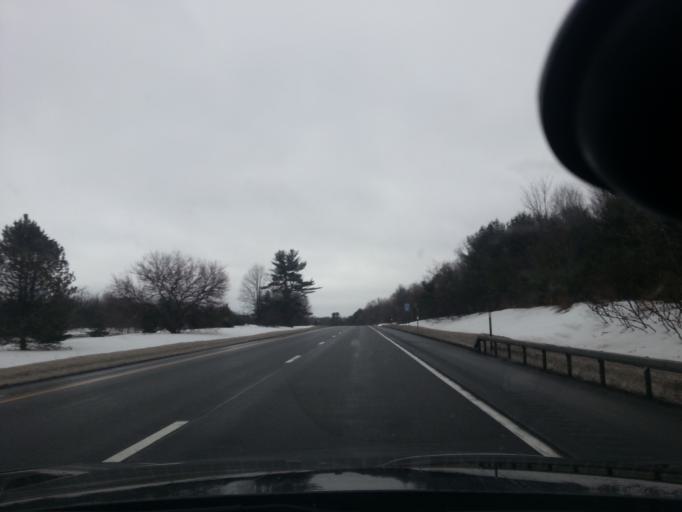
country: US
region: New York
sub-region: Oswego County
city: Central Square
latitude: 43.3233
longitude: -76.1269
